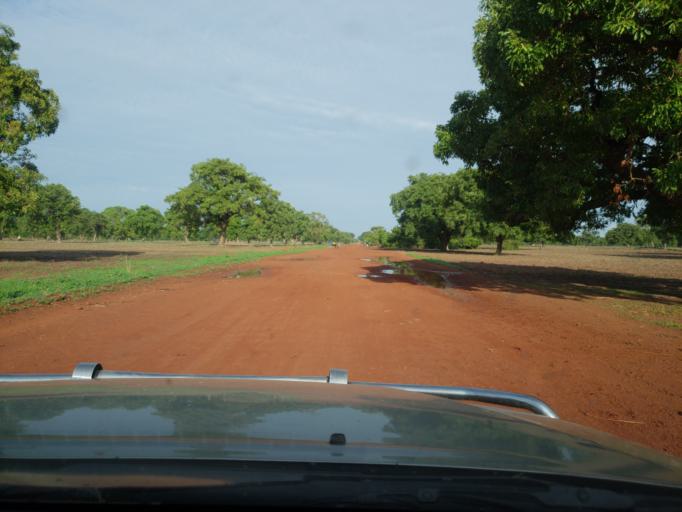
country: ML
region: Sikasso
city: Koutiala
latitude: 12.4199
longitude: -5.6982
